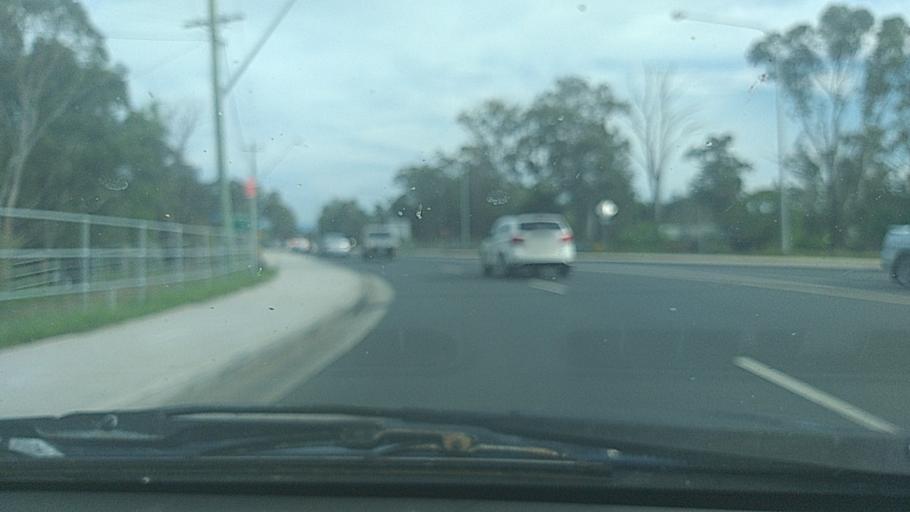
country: AU
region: New South Wales
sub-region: Hawkesbury
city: South Windsor
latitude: -33.6415
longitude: 150.7855
